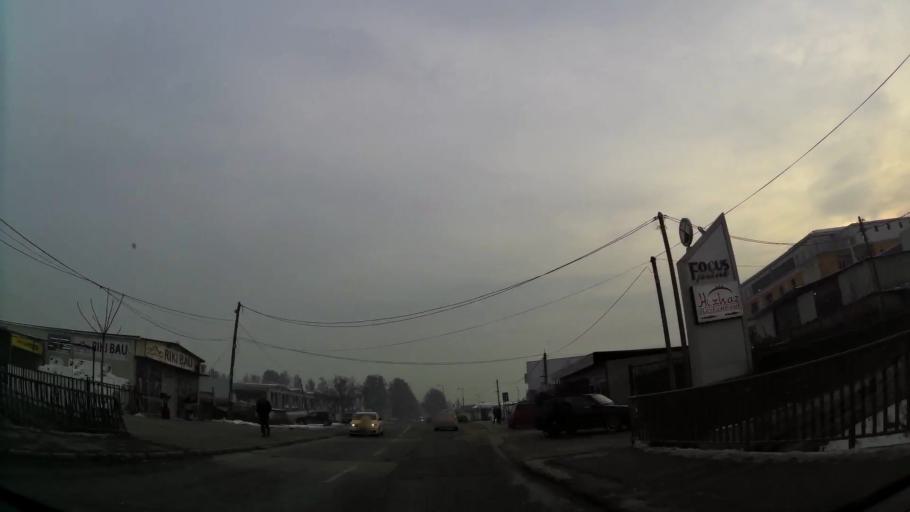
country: MK
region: Suto Orizari
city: Suto Orizare
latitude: 42.0269
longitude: 21.4294
